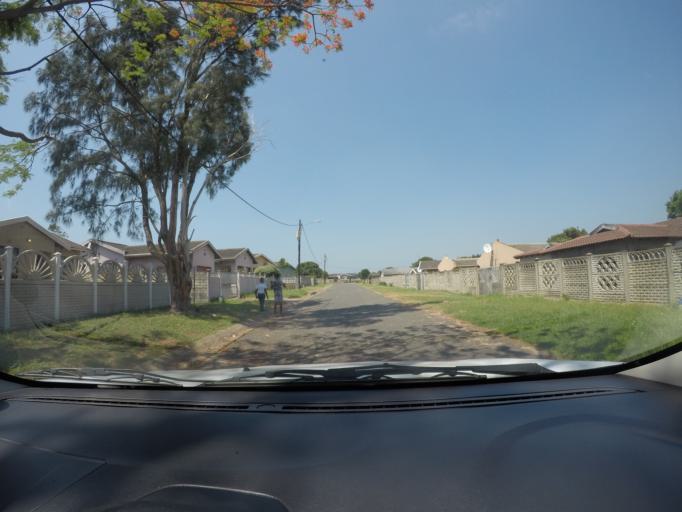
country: ZA
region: KwaZulu-Natal
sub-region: uThungulu District Municipality
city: eSikhawini
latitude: -28.8673
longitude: 31.9241
